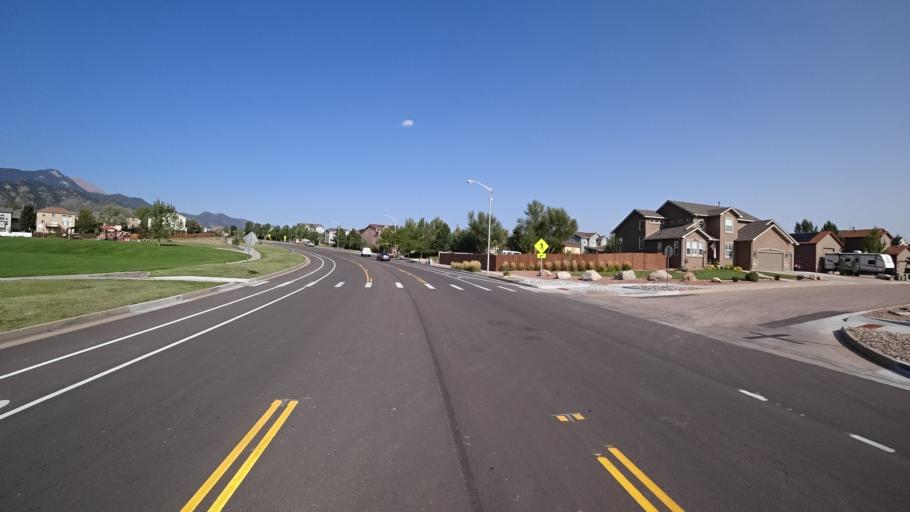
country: US
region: Colorado
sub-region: El Paso County
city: Colorado Springs
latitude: 38.8276
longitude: -104.8524
